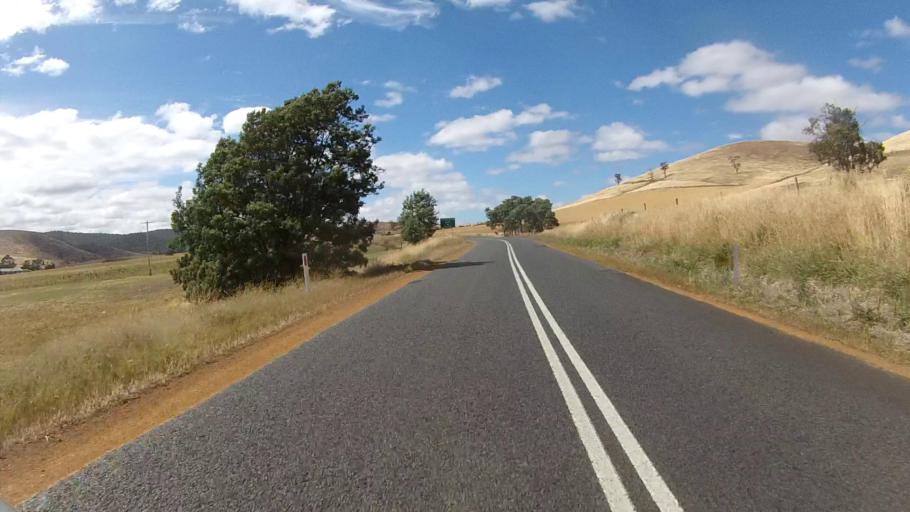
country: AU
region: Tasmania
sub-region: Brighton
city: Bridgewater
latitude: -42.5545
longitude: 147.3841
